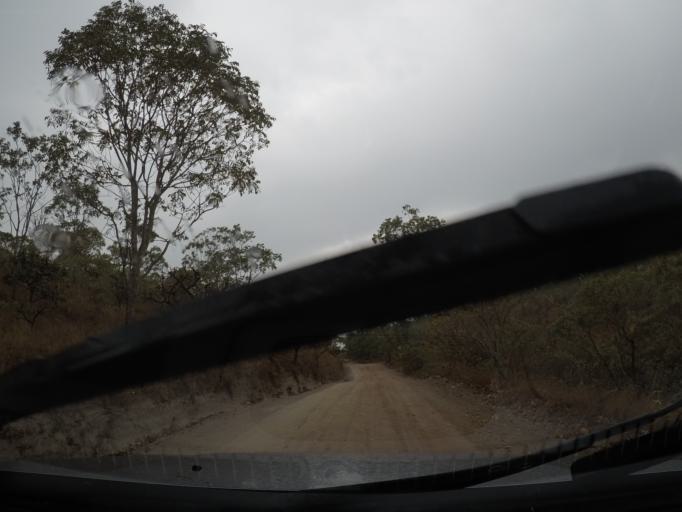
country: BR
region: Goias
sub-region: Pirenopolis
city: Pirenopolis
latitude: -15.8225
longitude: -48.8866
